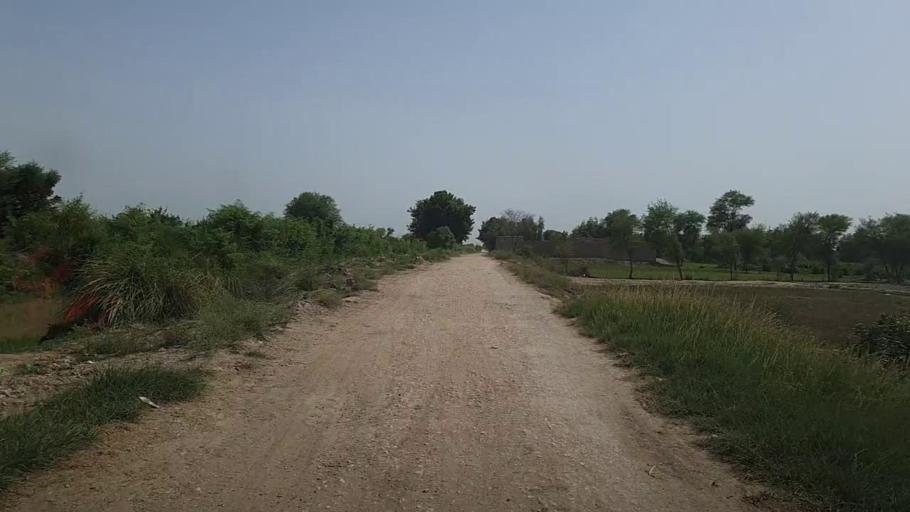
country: PK
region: Sindh
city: Pad Idan
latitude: 26.7949
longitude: 68.3294
